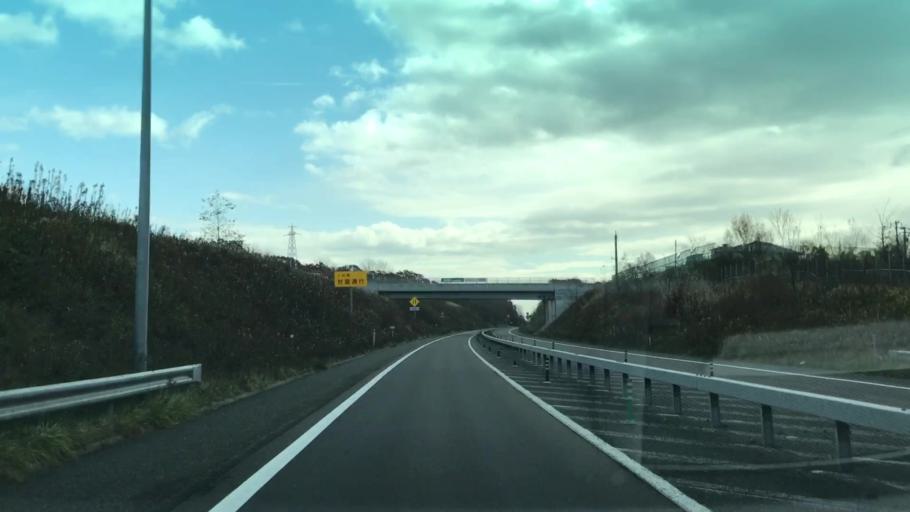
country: JP
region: Hokkaido
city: Shizunai-furukawacho
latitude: 42.5409
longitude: 142.0156
